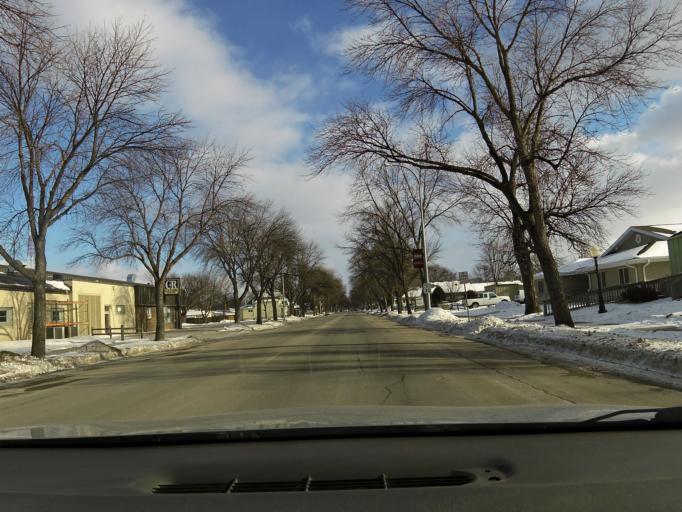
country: US
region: North Dakota
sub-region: Grand Forks County
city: Grand Forks
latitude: 47.9317
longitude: -97.0467
